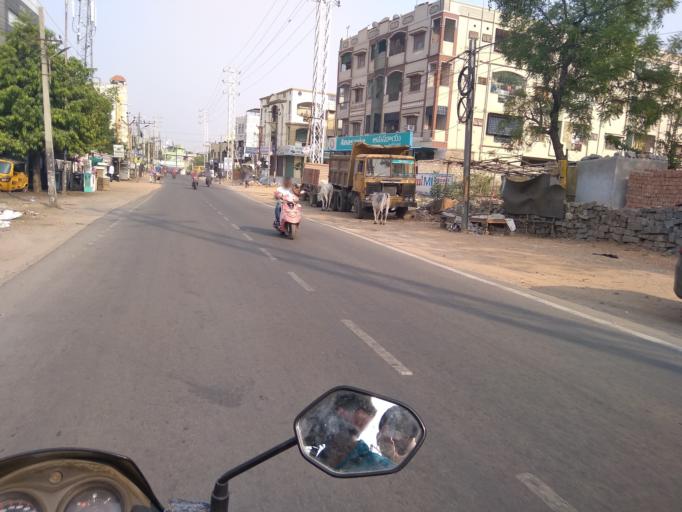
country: IN
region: Telangana
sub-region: Hyderabad
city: Malkajgiri
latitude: 17.4622
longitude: 78.5620
